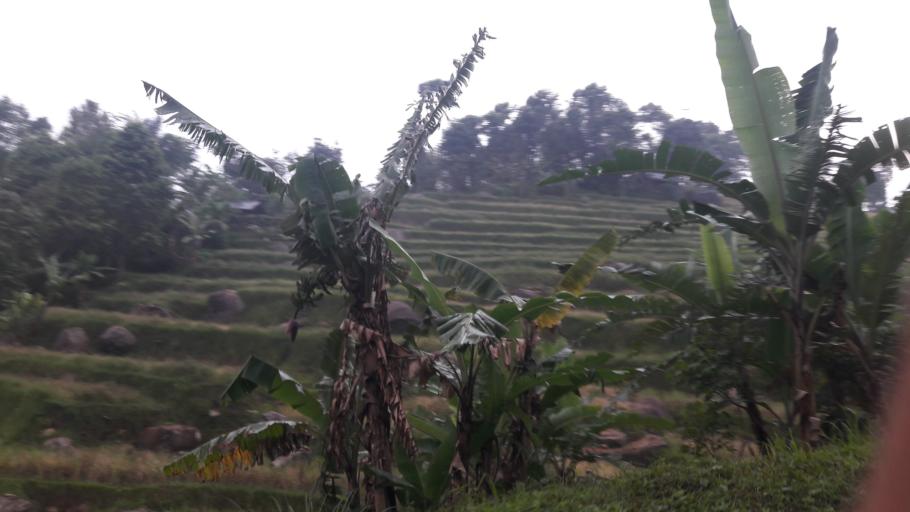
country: ID
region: West Java
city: Cipeundeuy
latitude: -6.6786
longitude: 106.5262
